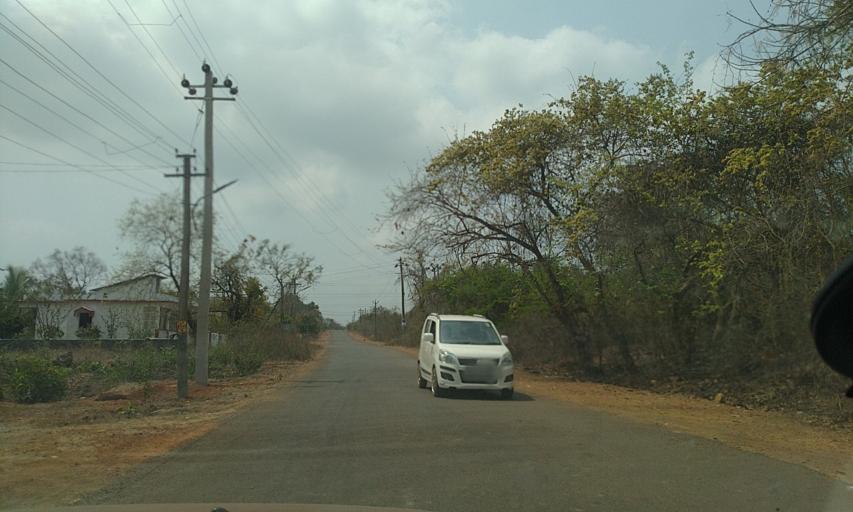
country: IN
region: Goa
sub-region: North Goa
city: Goa Velha
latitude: 15.4852
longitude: 73.9101
